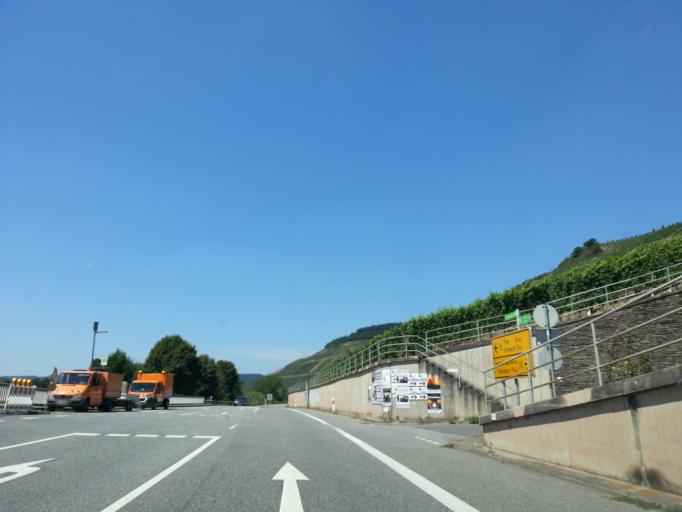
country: DE
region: Rheinland-Pfalz
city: Longuich
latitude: 49.8079
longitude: 6.7788
